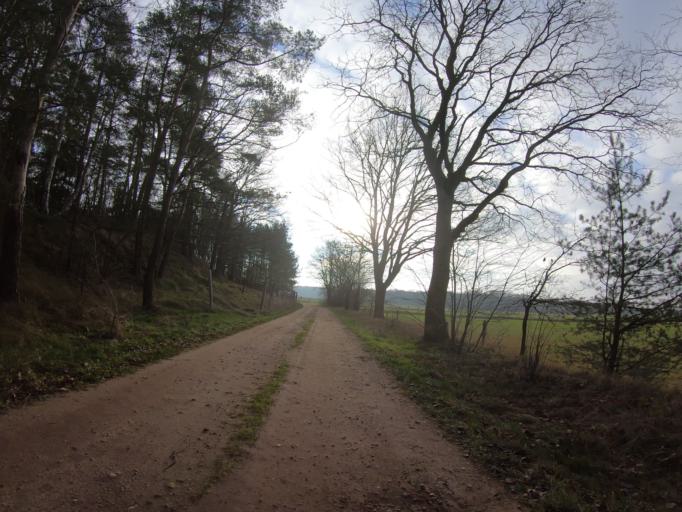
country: DE
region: Lower Saxony
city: Ribbesbuttel
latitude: 52.4826
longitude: 10.4839
